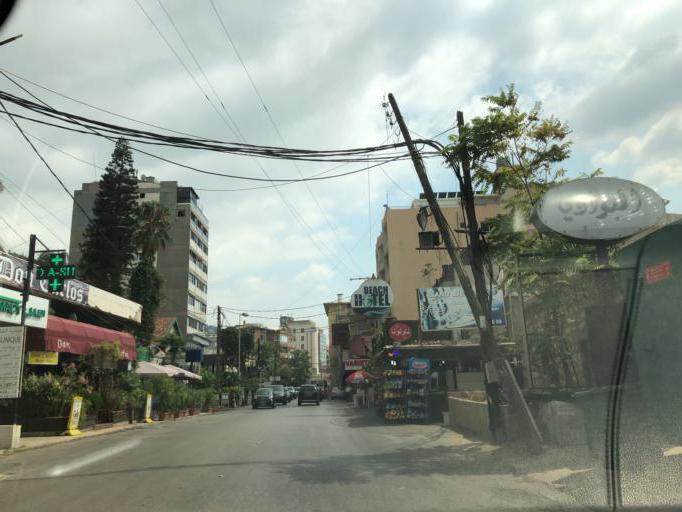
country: LB
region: Mont-Liban
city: Djounie
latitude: 33.9905
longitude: 35.6387
